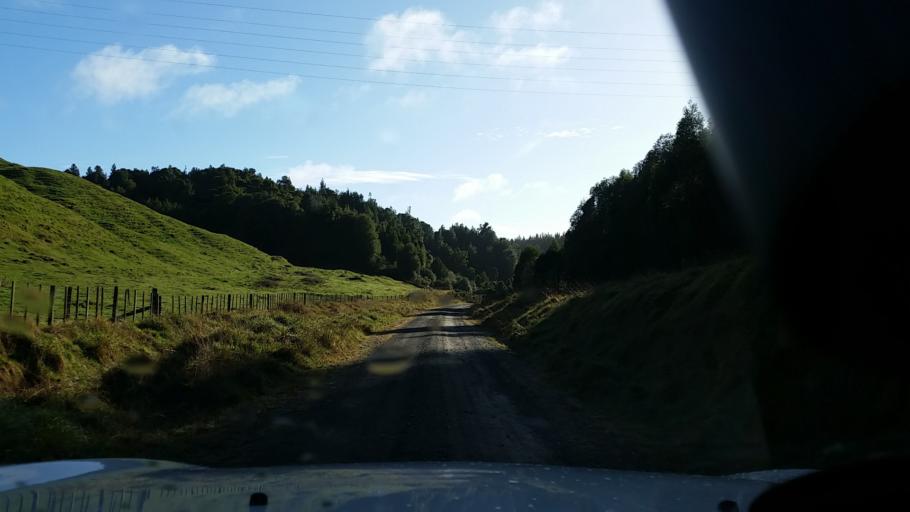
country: NZ
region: Bay of Plenty
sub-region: Kawerau District
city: Kawerau
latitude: -38.0119
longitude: 176.5973
